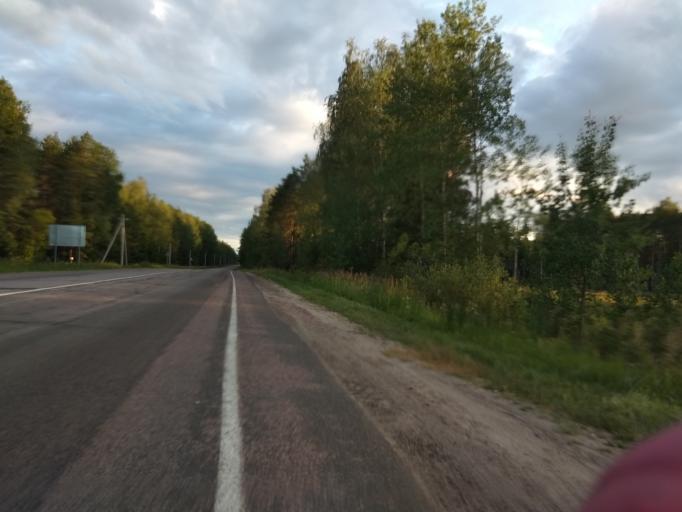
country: RU
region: Moskovskaya
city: Misheronskiy
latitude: 55.6180
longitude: 39.7255
